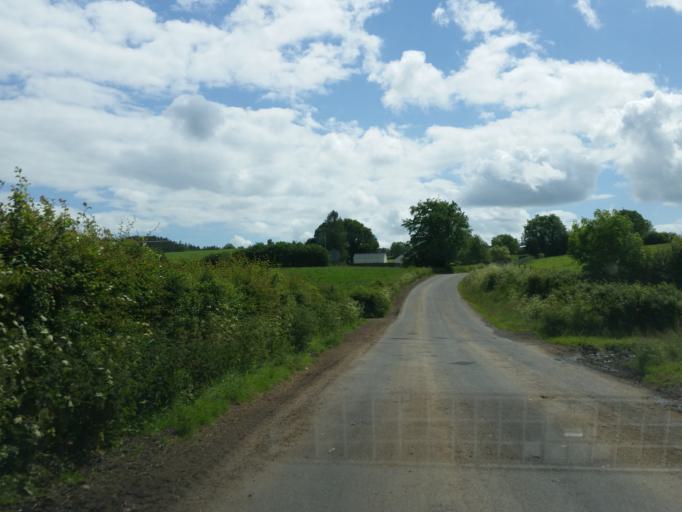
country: GB
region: Northern Ireland
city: Fivemiletown
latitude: 54.3628
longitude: -7.3078
